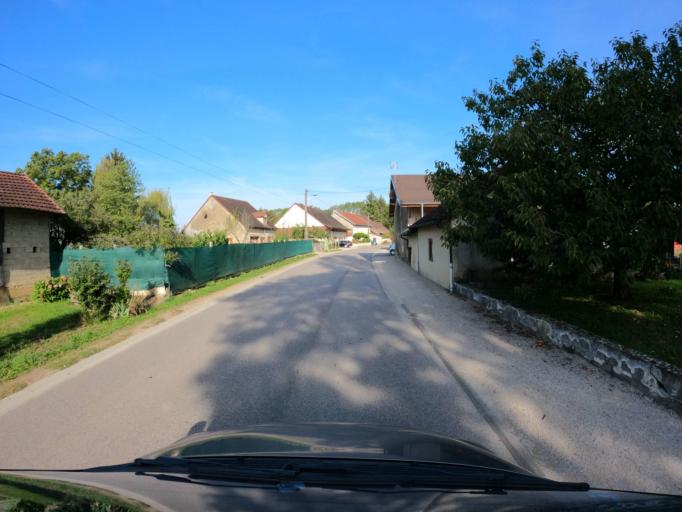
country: FR
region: Franche-Comte
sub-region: Departement du Jura
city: Bletterans
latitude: 46.7415
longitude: 5.4977
